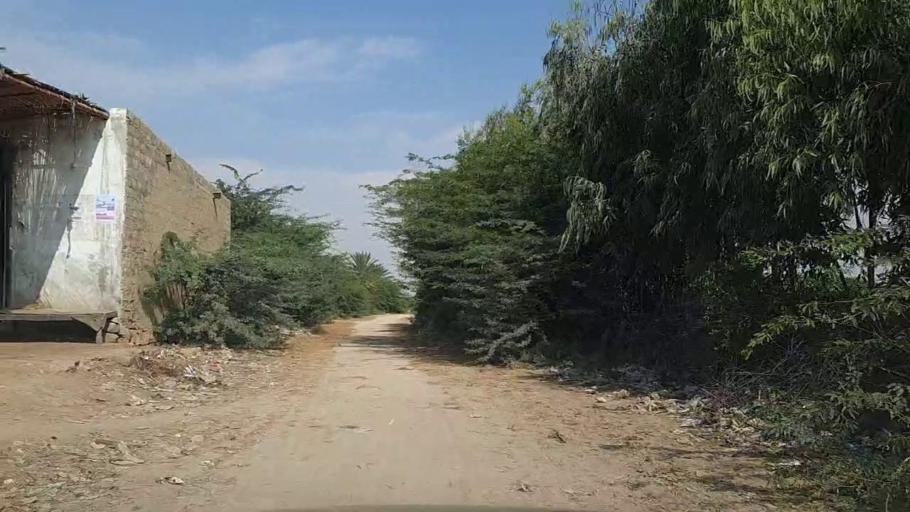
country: PK
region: Sindh
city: Thatta
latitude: 24.7985
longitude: 67.8510
